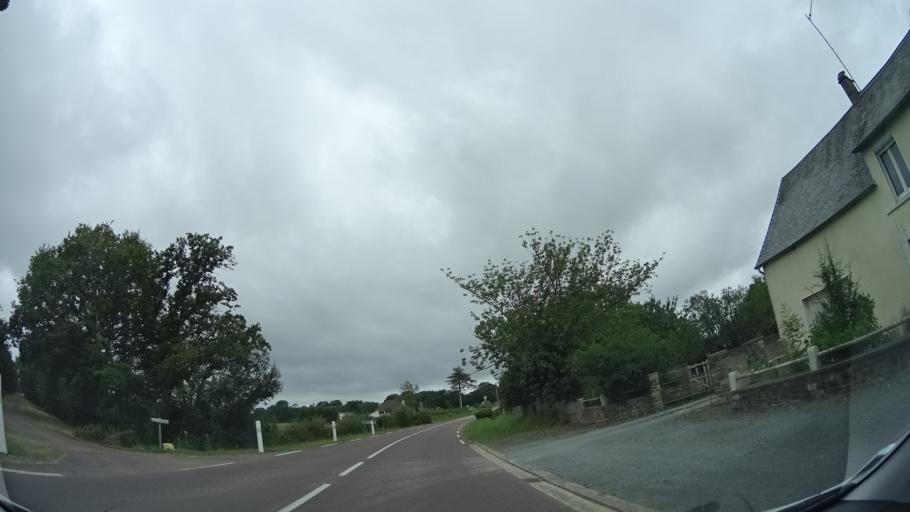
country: FR
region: Lower Normandy
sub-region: Departement de la Manche
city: La Haye-du-Puits
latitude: 49.3017
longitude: -1.5807
